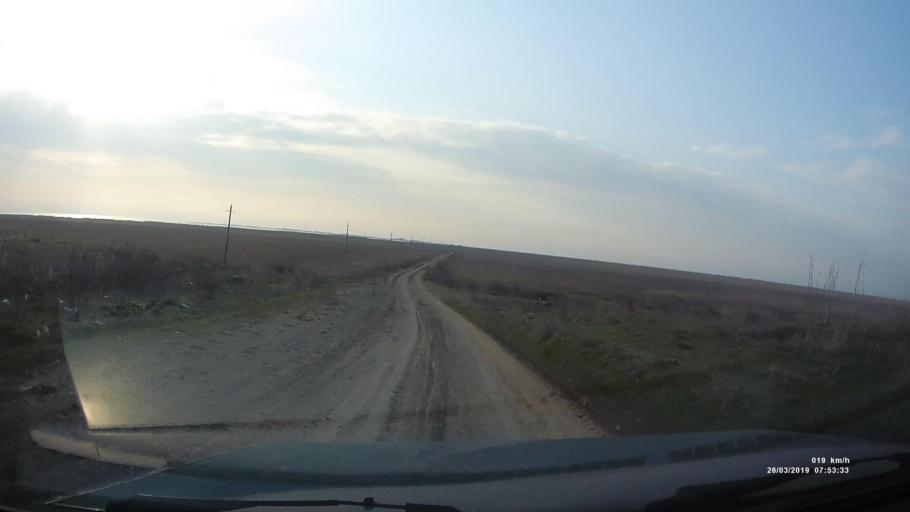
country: RU
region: Krasnodarskiy
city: Shabel'skoye
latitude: 47.1353
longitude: 38.5489
